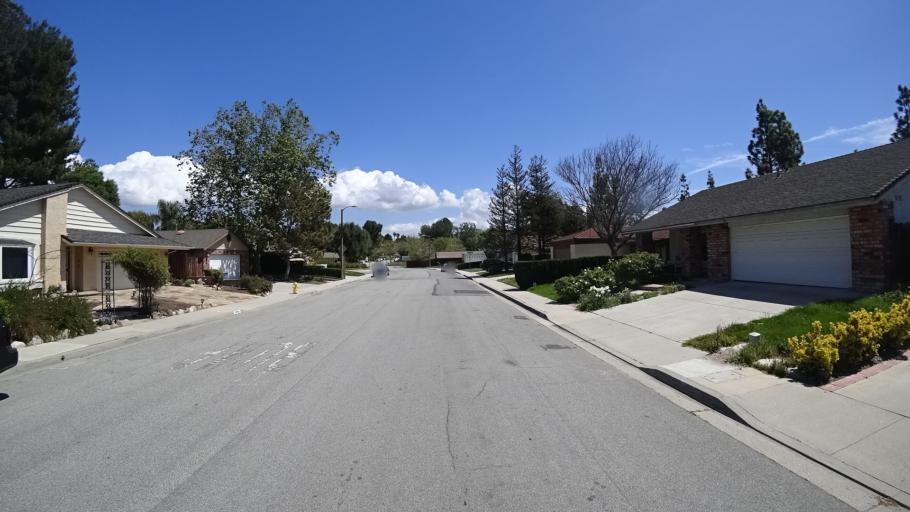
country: US
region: California
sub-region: Ventura County
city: Thousand Oaks
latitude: 34.2131
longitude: -118.8466
